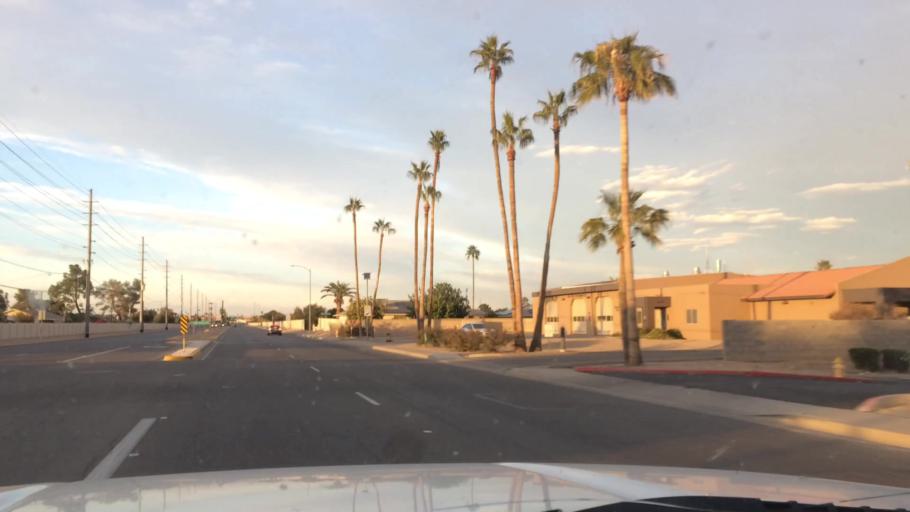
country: US
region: Arizona
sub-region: Maricopa County
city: Sun City
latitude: 33.5871
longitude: -112.2726
